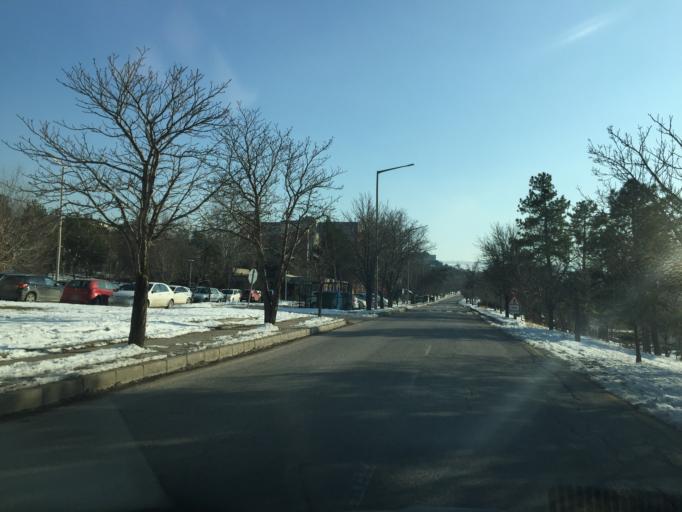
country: TR
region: Ankara
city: Ankara
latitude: 39.8967
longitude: 32.7806
